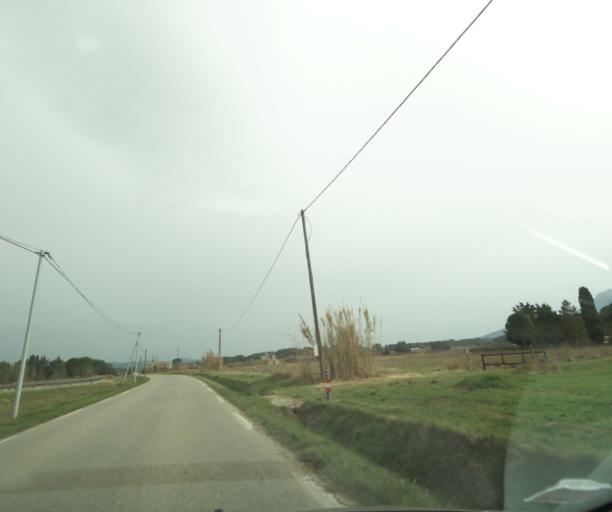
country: FR
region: Provence-Alpes-Cote d'Azur
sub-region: Departement des Bouches-du-Rhone
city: Trets
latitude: 43.4636
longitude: 5.7021
